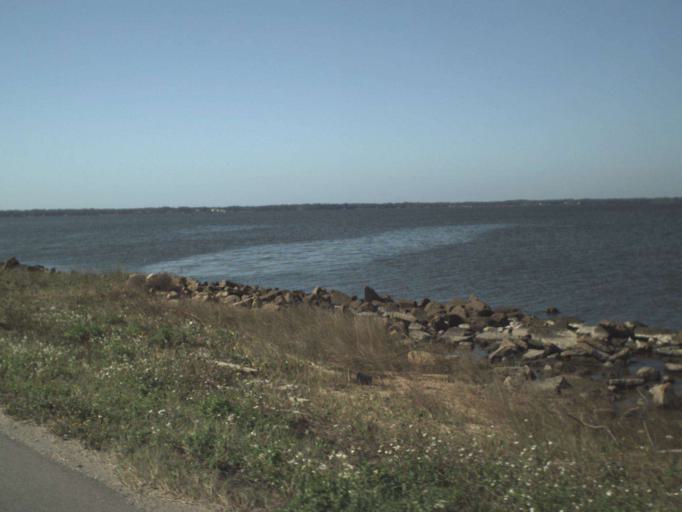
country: US
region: Florida
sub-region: Walton County
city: Freeport
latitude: 30.4186
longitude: -86.1601
